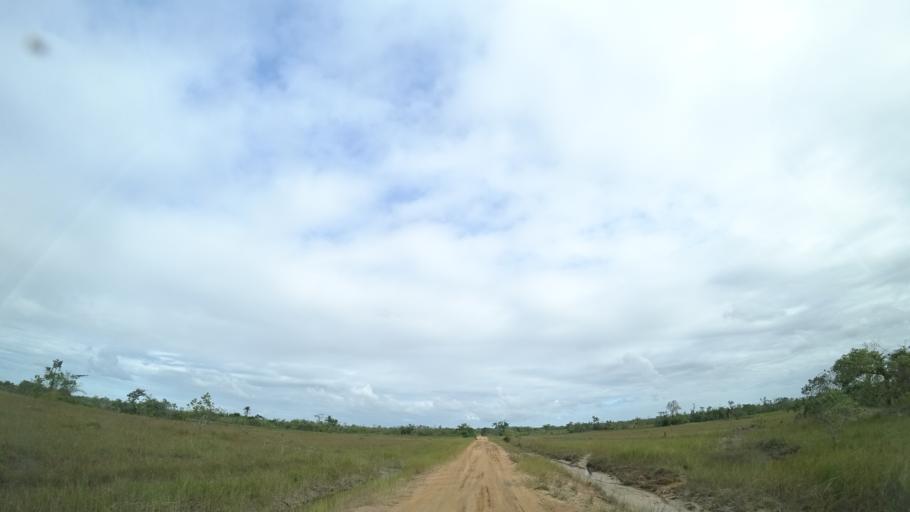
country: MZ
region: Sofala
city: Dondo
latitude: -19.5825
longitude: 35.0868
